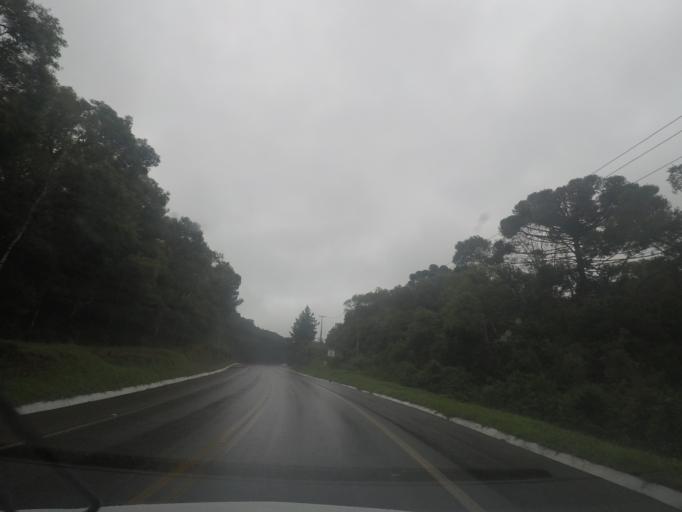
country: BR
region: Parana
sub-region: Colombo
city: Colombo
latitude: -25.3163
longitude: -49.1586
